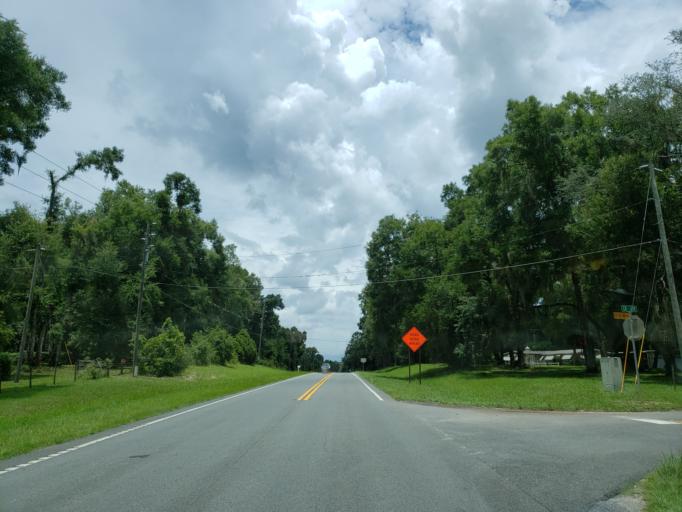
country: US
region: Florida
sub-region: Citrus County
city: Floral City
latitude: 28.6426
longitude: -82.2511
